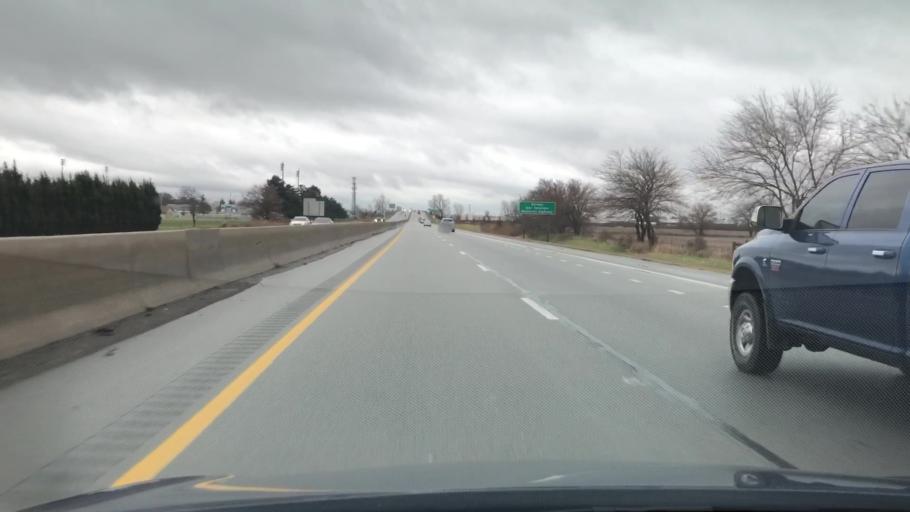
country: US
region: Ohio
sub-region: Wood County
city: Northwood
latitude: 41.6062
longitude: -83.4763
